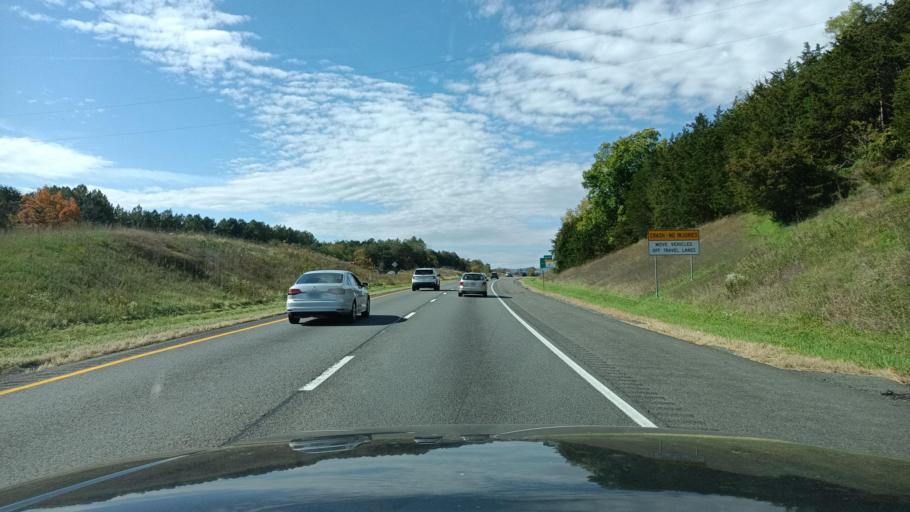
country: US
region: Virginia
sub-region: Shenandoah County
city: Strasburg
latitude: 39.0053
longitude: -78.3237
